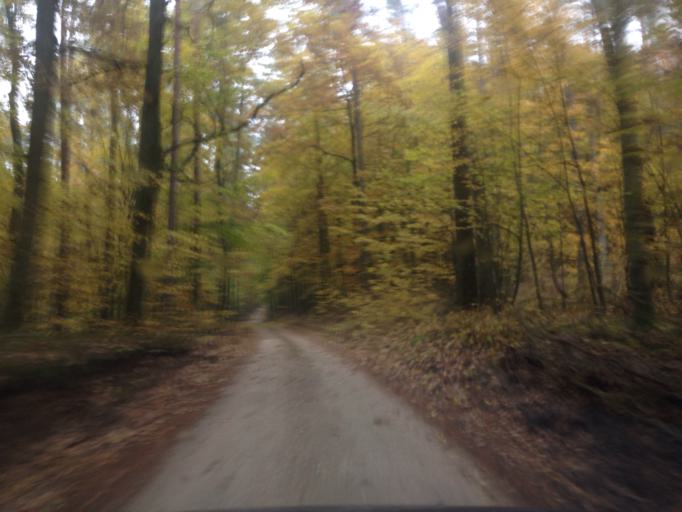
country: PL
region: Kujawsko-Pomorskie
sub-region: Powiat brodnicki
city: Gorzno
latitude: 53.2292
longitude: 19.7035
